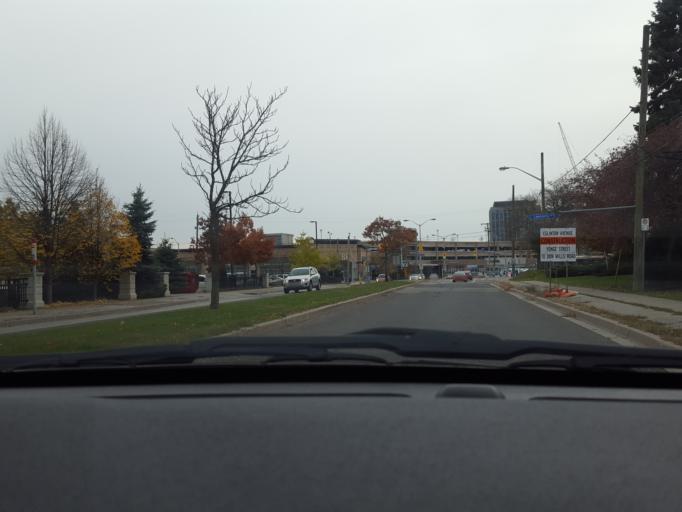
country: CA
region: Ontario
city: Willowdale
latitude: 43.7376
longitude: -79.3470
